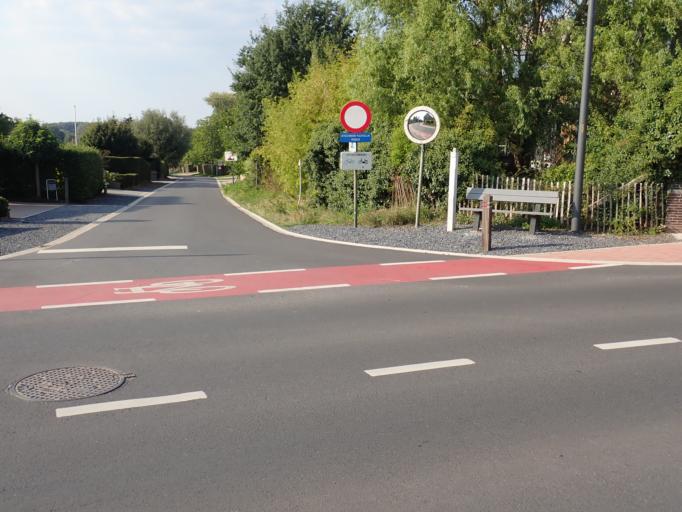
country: BE
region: Flanders
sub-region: Provincie Vlaams-Brabant
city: Opwijk
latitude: 50.9555
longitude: 4.1709
